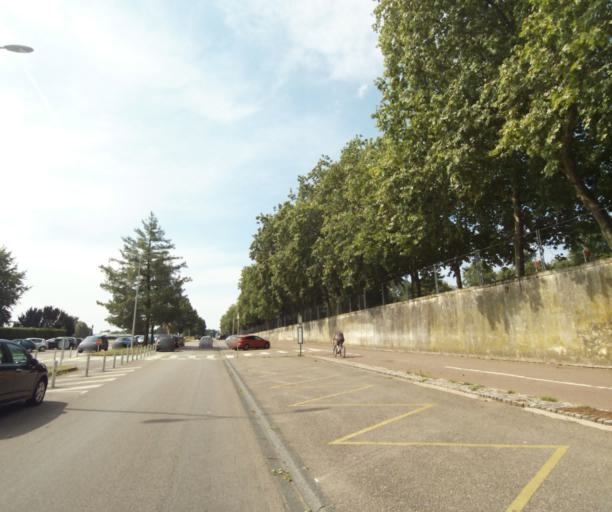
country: FR
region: Lorraine
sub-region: Departement de Meurthe-et-Moselle
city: Luneville
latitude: 48.5965
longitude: 6.5029
